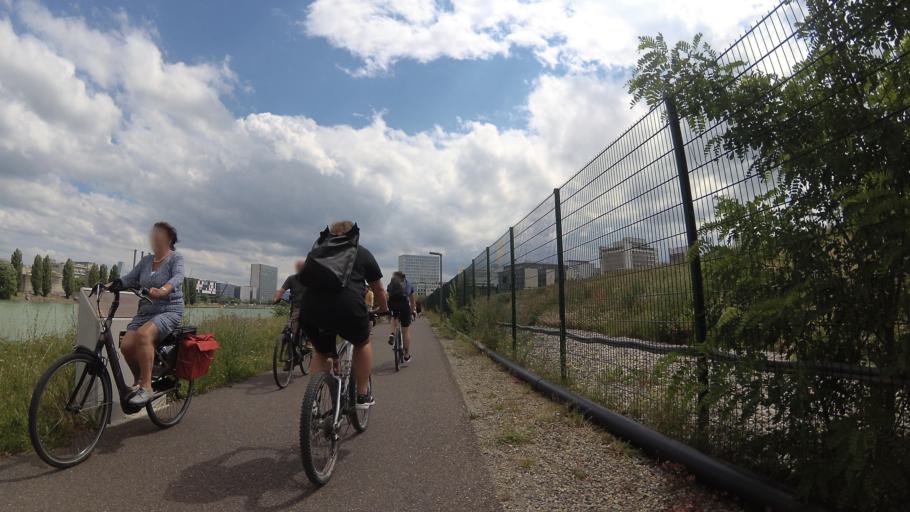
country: FR
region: Alsace
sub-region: Departement du Haut-Rhin
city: Village-Neuf
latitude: 47.5781
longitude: 7.5828
